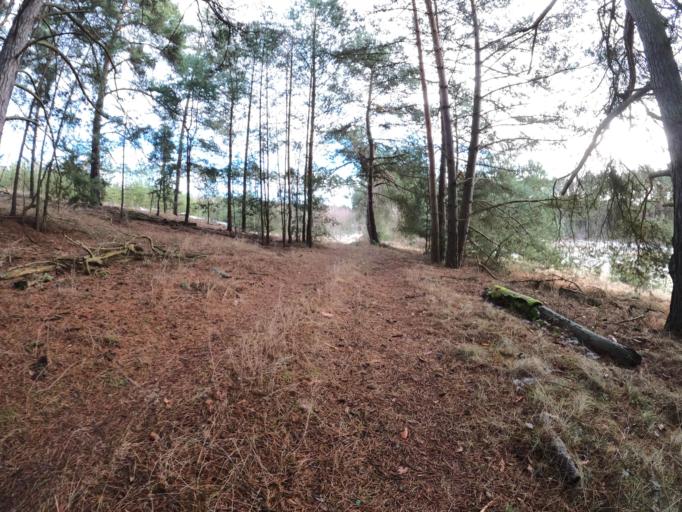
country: PL
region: Lubusz
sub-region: Powiat slubicki
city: Cybinka
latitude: 52.2582
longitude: 14.7962
